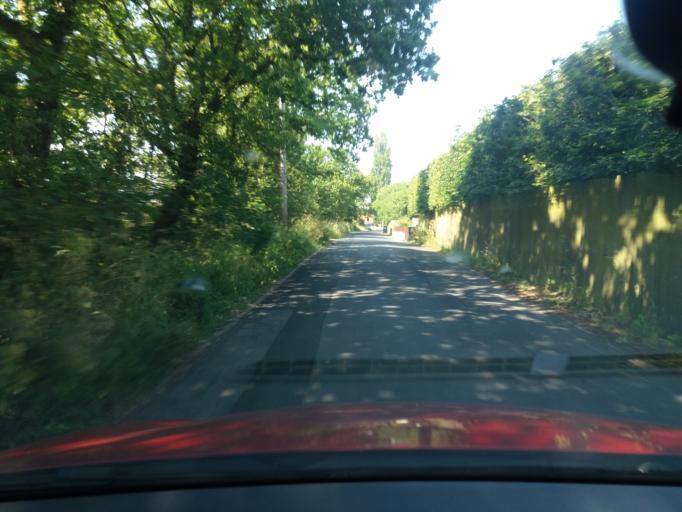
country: GB
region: England
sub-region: Lancashire
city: Euxton
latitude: 53.6706
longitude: -2.6671
